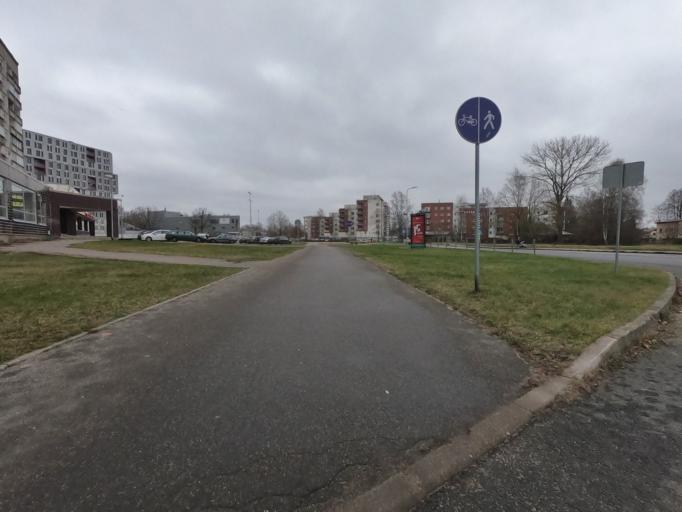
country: LV
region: Marupe
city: Marupe
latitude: 56.9445
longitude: 24.0152
